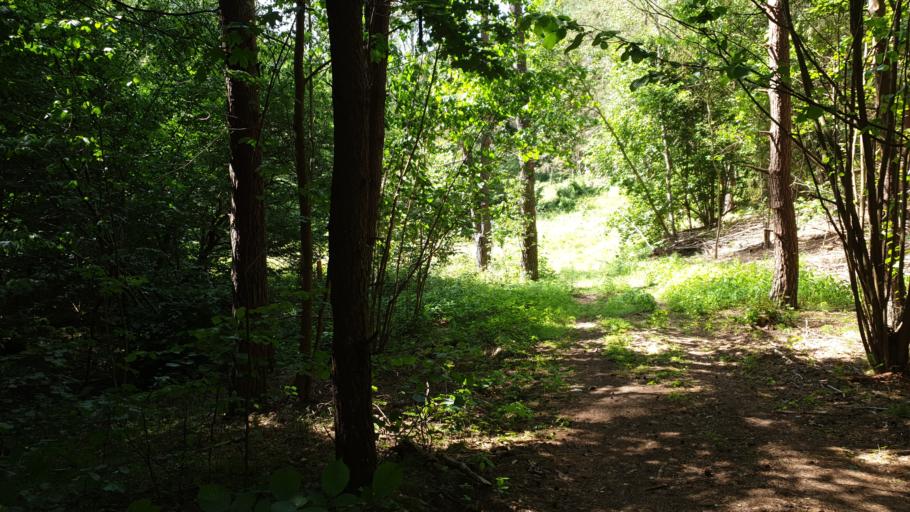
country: LT
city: Grigiskes
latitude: 54.7819
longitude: 24.9916
